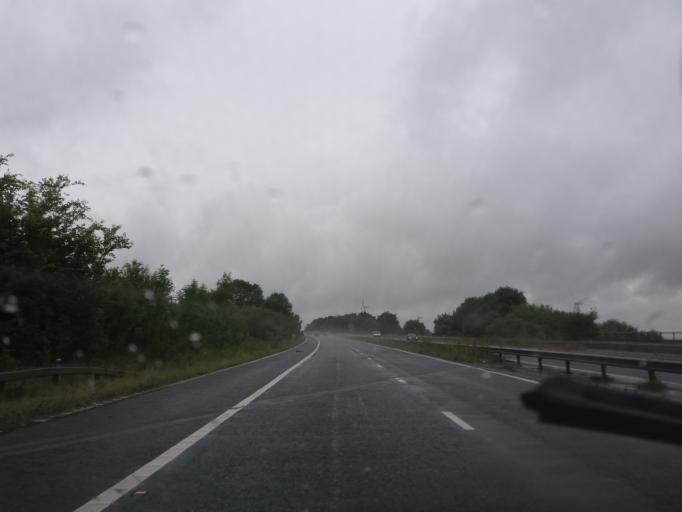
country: GB
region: England
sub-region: Rotherham
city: Bramley
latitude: 53.3958
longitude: -1.2697
